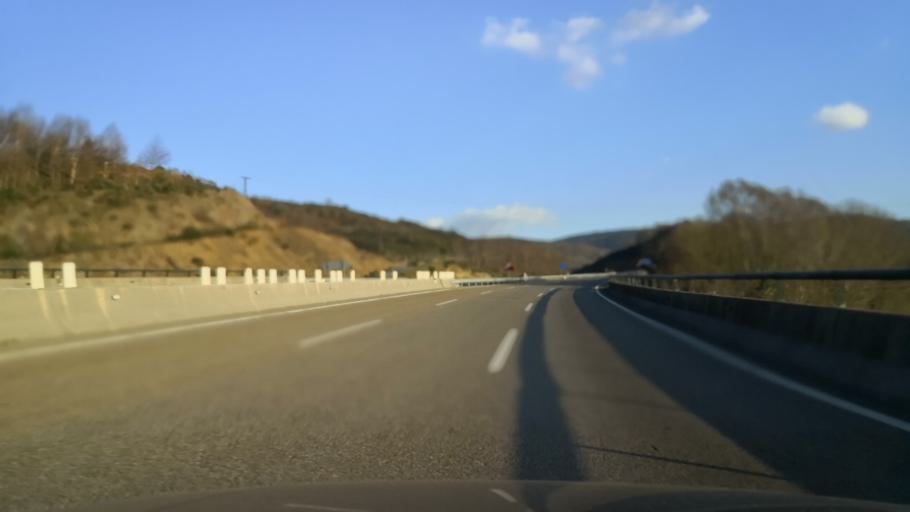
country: ES
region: Galicia
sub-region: Provincia de Lugo
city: San Roman
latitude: 42.7481
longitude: -7.0574
